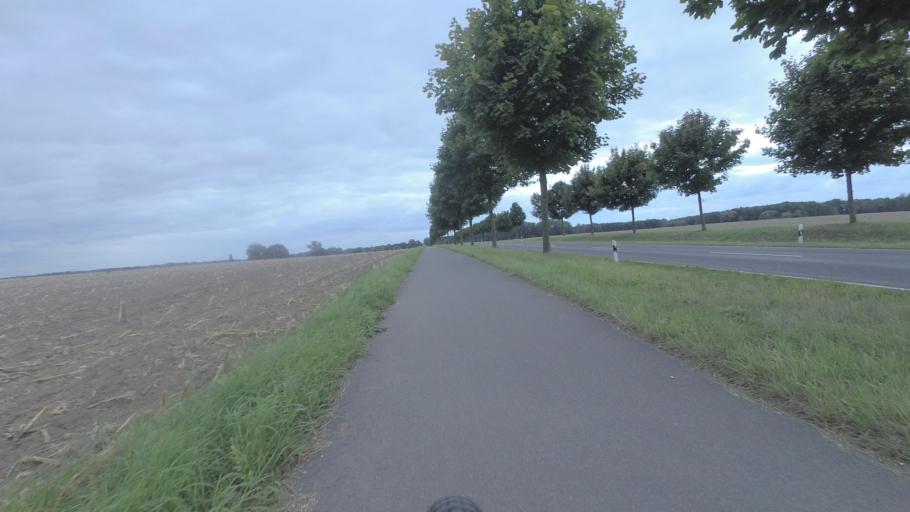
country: DE
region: Brandenburg
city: Werneuchen
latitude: 52.6063
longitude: 13.6840
